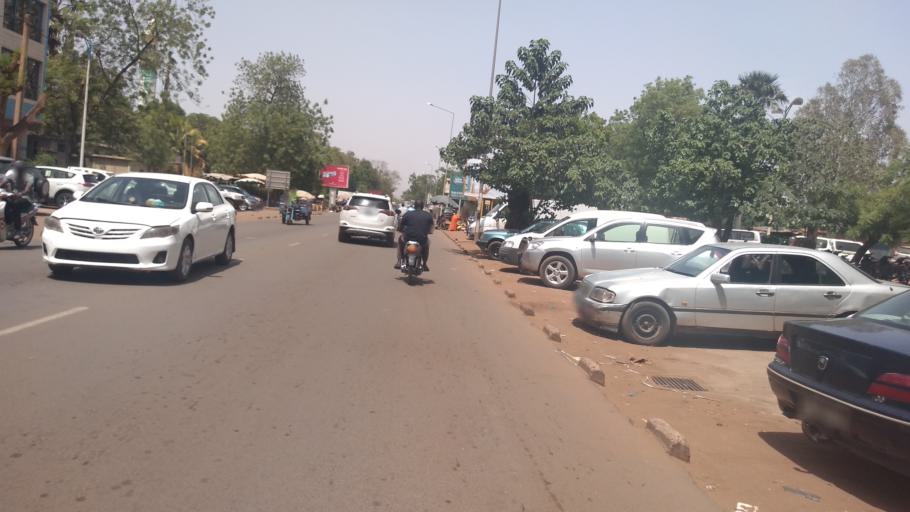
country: ML
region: Bamako
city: Bamako
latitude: 12.6426
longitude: -8.0196
